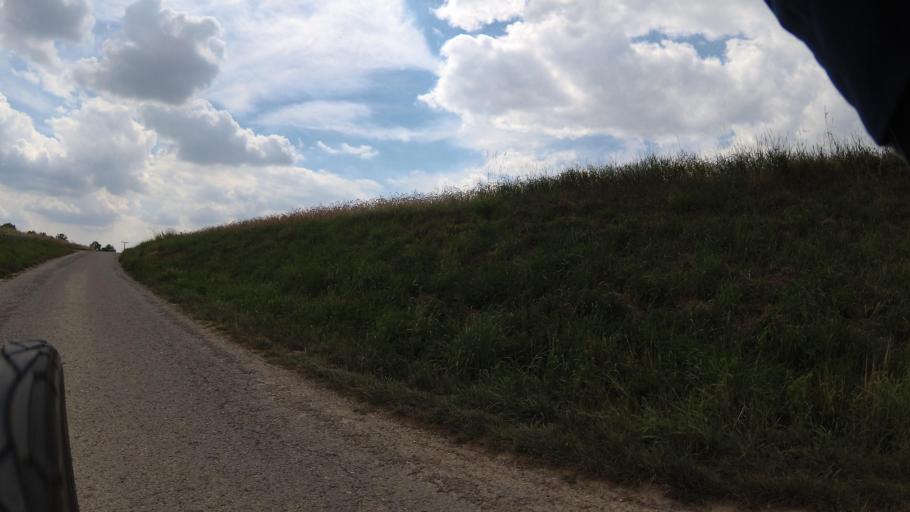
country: DE
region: Baden-Wuerttemberg
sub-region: Regierungsbezirk Stuttgart
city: Neudenau
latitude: 49.2738
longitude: 9.2732
